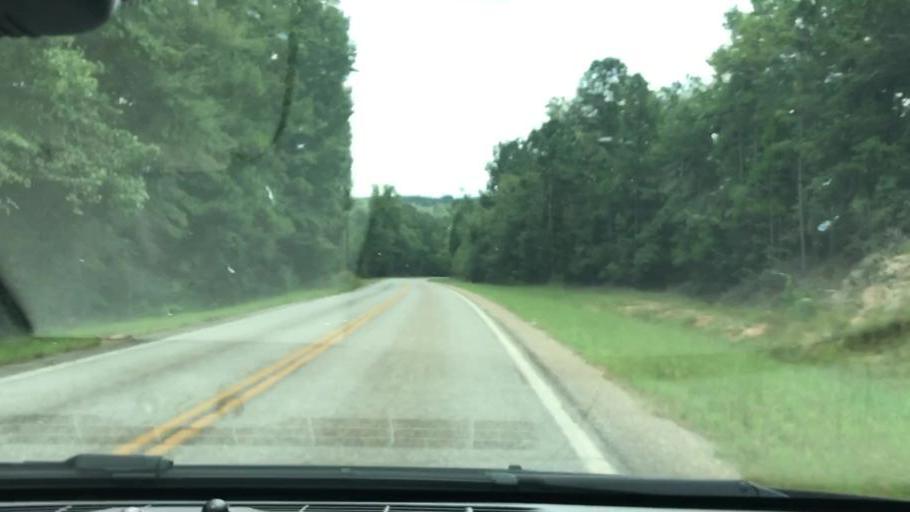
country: US
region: Georgia
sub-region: Stewart County
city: Lumpkin
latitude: 32.0584
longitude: -84.8163
